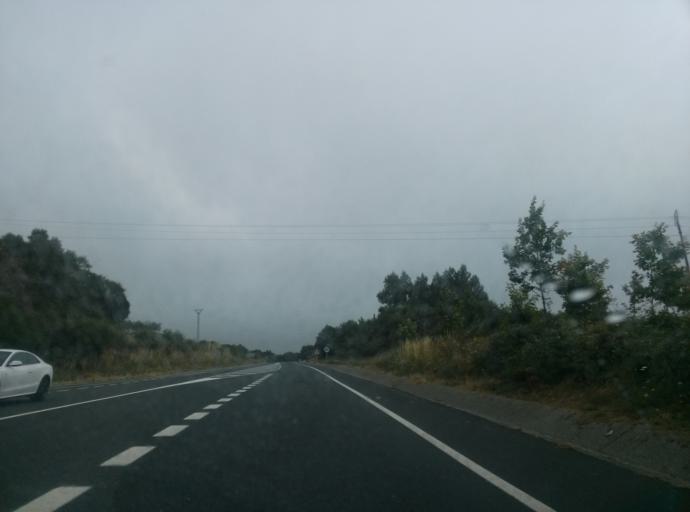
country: ES
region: Galicia
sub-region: Provincia de Lugo
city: Muras
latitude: 43.4317
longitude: -7.7527
